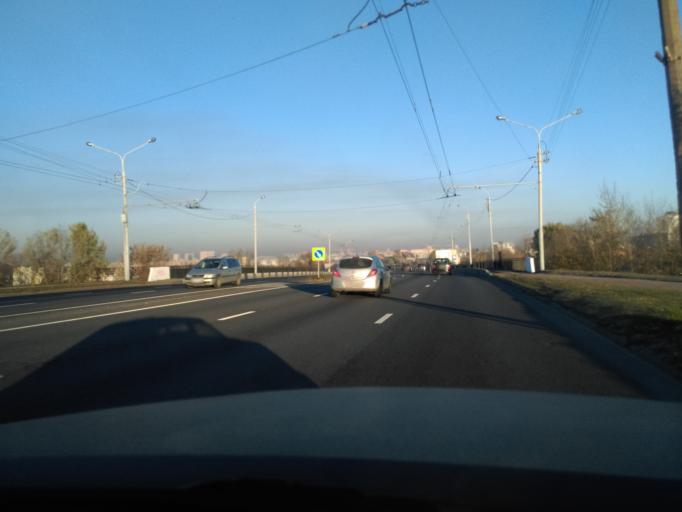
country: BY
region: Minsk
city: Minsk
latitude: 53.9032
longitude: 27.6365
